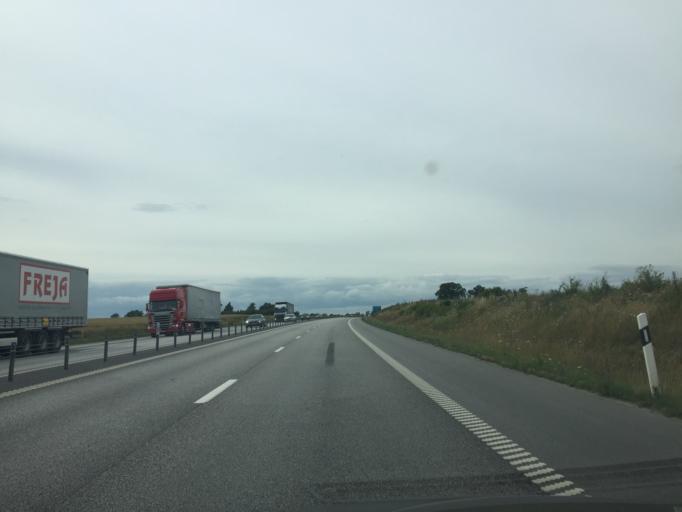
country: SE
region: Skane
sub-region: Trelleborgs Kommun
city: Skare
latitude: 55.4239
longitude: 13.0562
